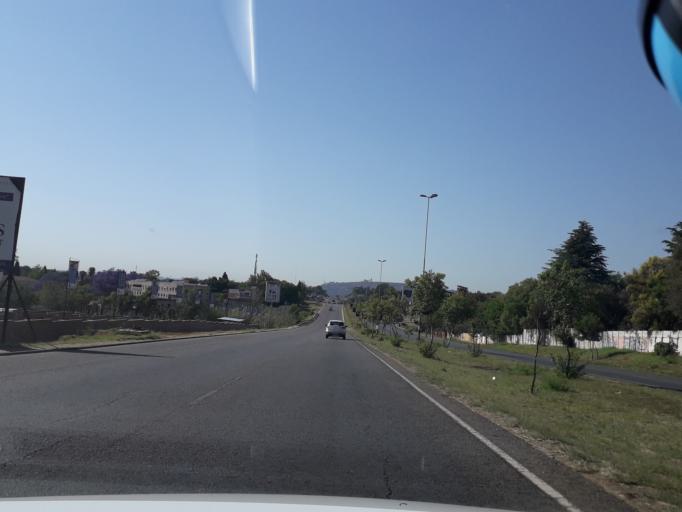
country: ZA
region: Gauteng
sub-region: City of Johannesburg Metropolitan Municipality
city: Roodepoort
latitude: -26.0878
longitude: 27.9360
